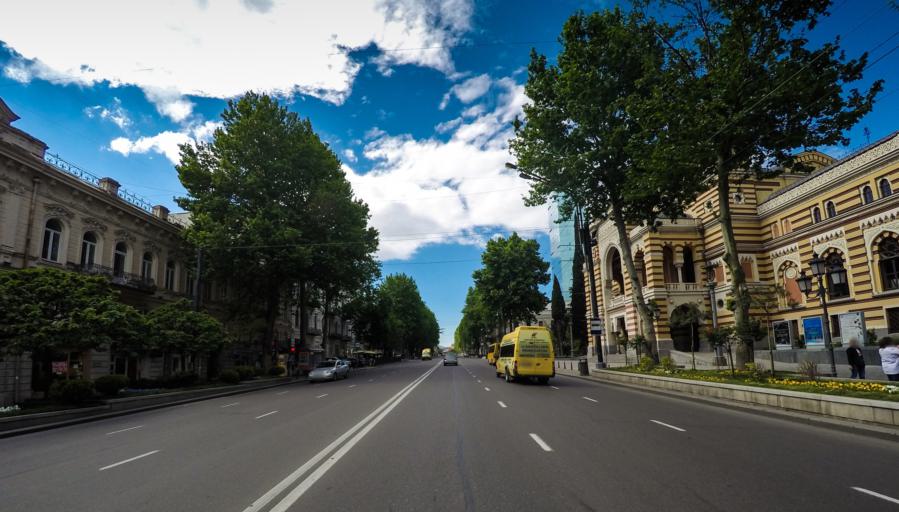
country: GE
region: T'bilisi
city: Tbilisi
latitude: 41.7005
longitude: 44.7960
